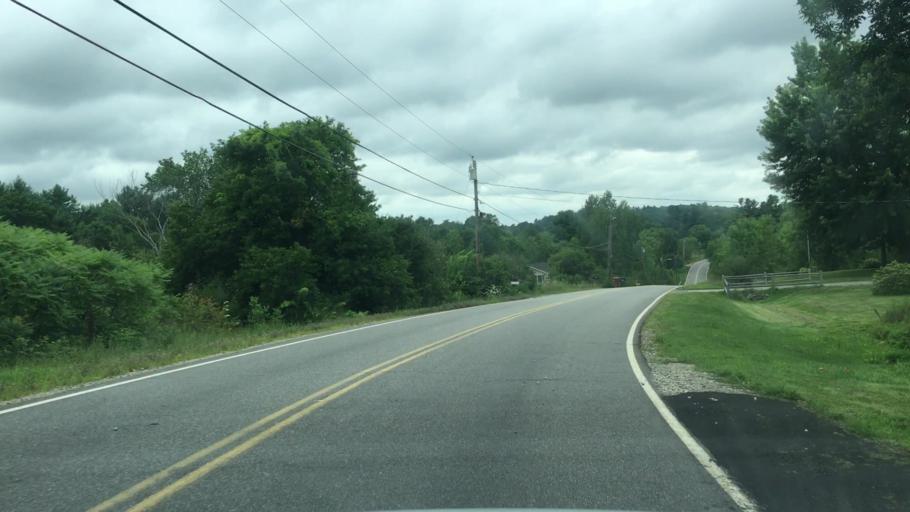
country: US
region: Maine
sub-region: York County
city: Dayton
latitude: 43.5203
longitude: -70.5177
